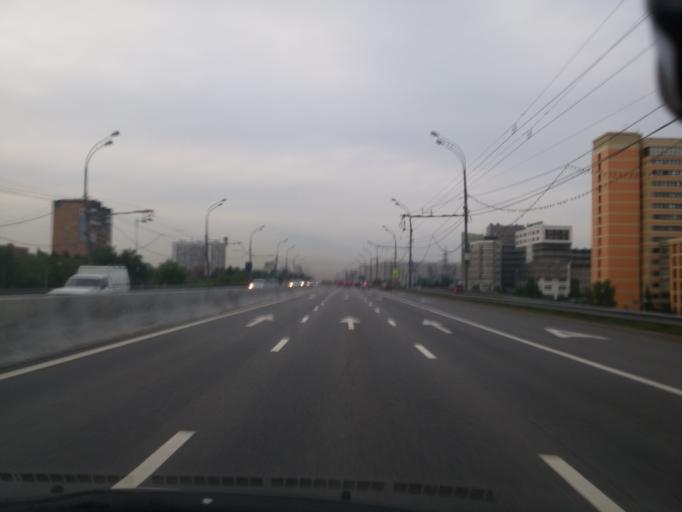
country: RU
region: Moscow
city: Slobodka
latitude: 55.8732
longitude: 37.5861
